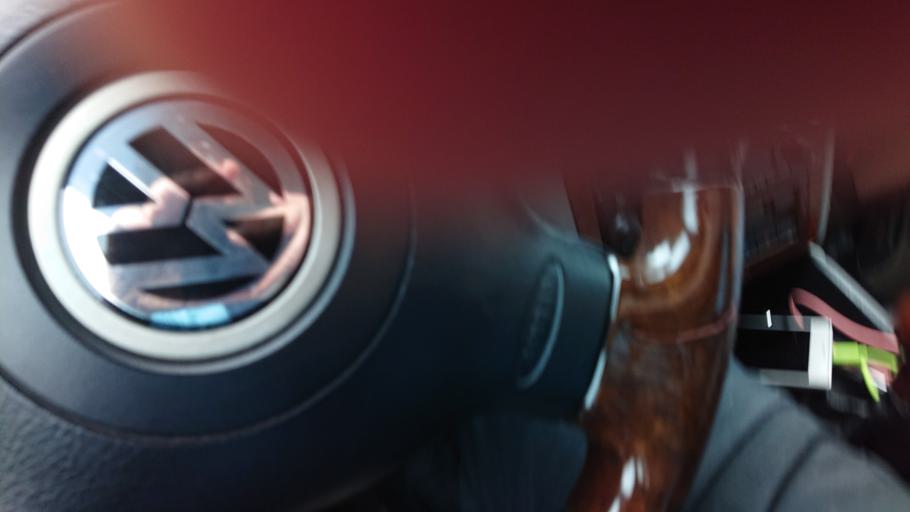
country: NO
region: Rogaland
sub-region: Hjelmeland
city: Hjelmelandsvagen
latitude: 59.2345
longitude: 6.1865
